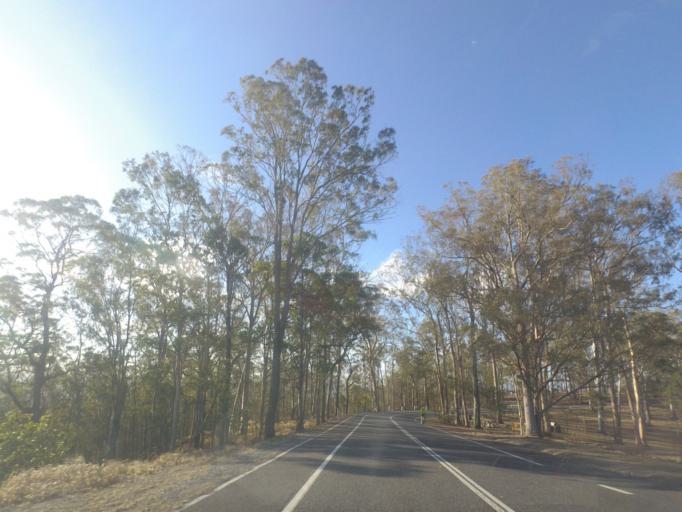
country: AU
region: Queensland
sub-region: Brisbane
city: Kenmore Hills
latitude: -27.4711
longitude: 152.9415
